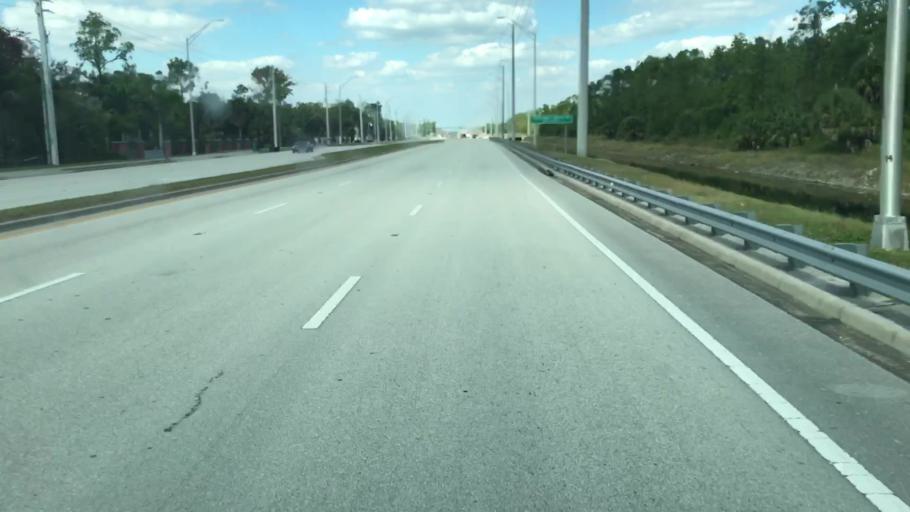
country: US
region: Florida
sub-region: Collier County
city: Vineyards
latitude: 26.2386
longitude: -81.6878
